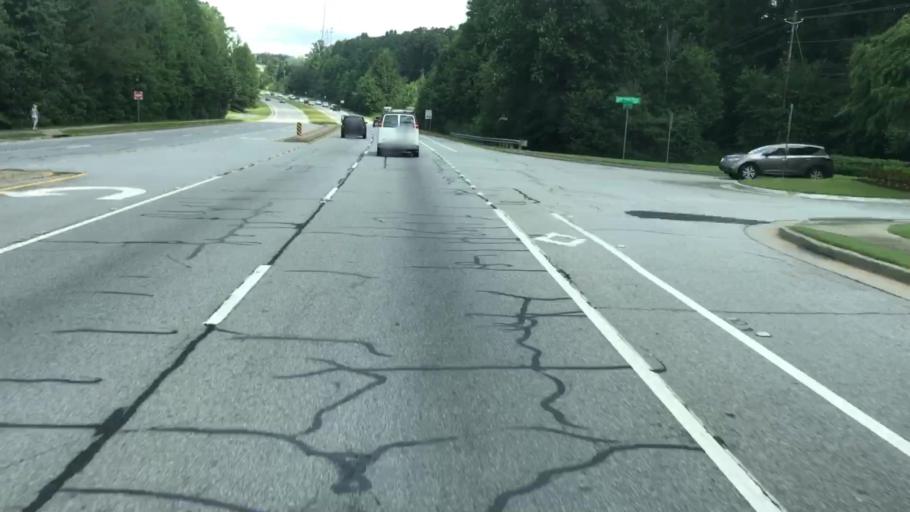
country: US
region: Georgia
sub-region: Gwinnett County
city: Suwanee
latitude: 33.9810
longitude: -84.0755
